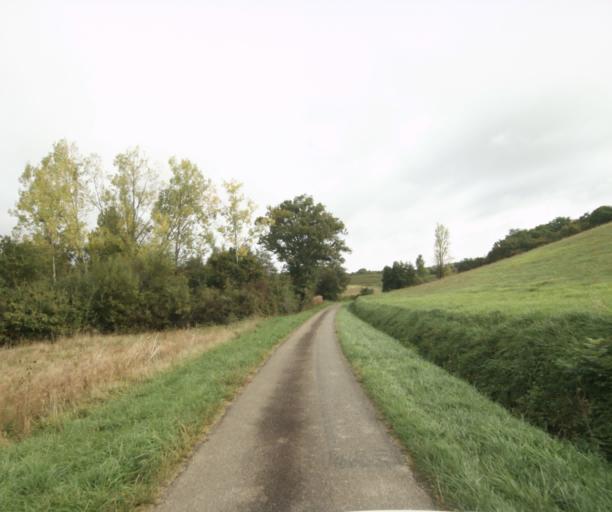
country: FR
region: Midi-Pyrenees
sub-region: Departement du Gers
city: Nogaro
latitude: 43.8264
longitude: -0.0800
